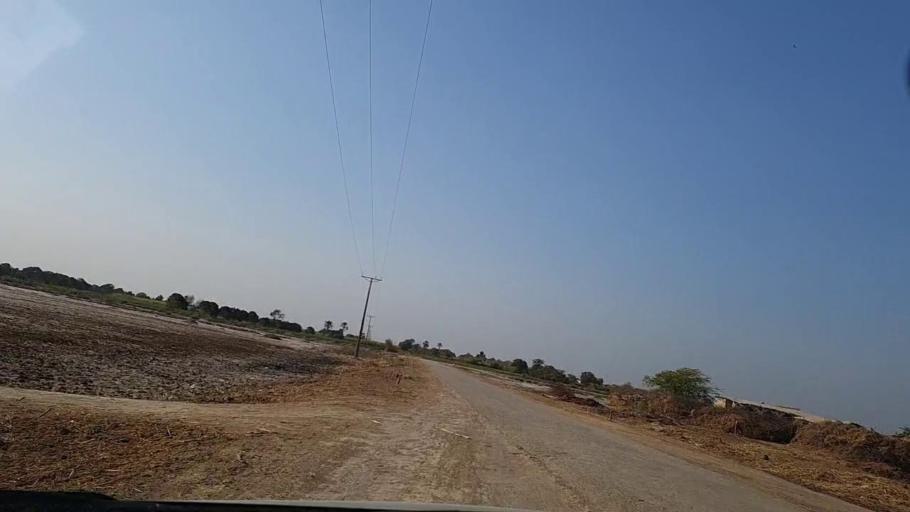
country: PK
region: Sindh
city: Mirwah Gorchani
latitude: 25.2179
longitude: 68.9921
